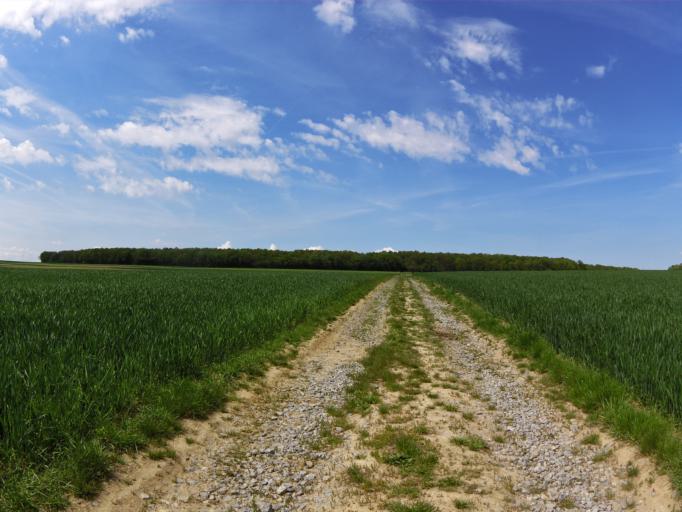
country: DE
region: Bavaria
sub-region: Regierungsbezirk Unterfranken
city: Theilheim
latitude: 49.7378
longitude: 10.0372
